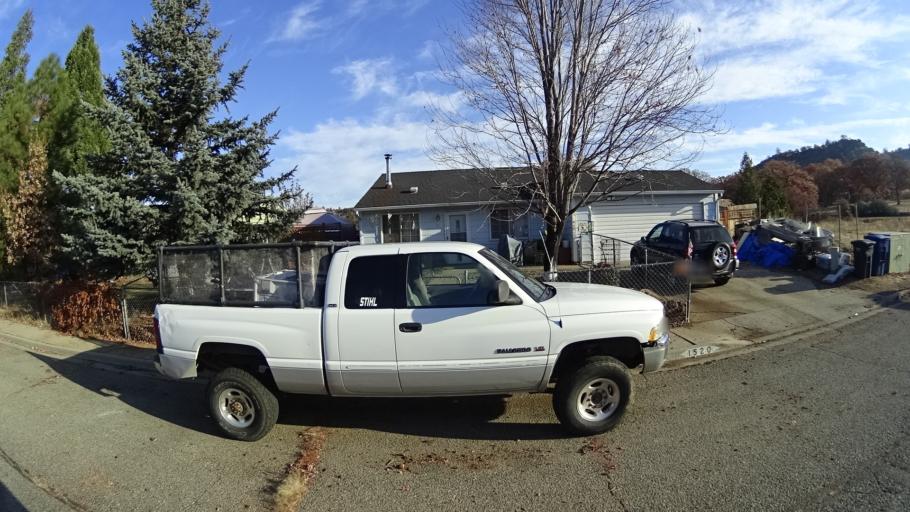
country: US
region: California
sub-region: Siskiyou County
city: Yreka
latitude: 41.7081
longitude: -122.6201
